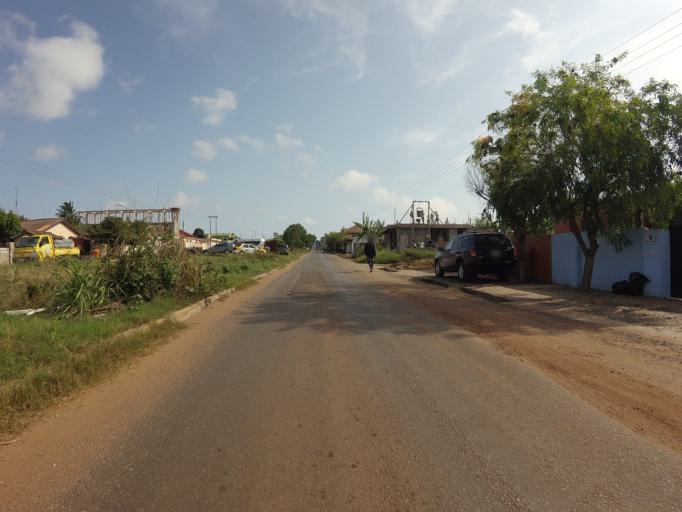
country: GH
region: Greater Accra
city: Nungua
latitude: 5.6404
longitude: -0.1007
